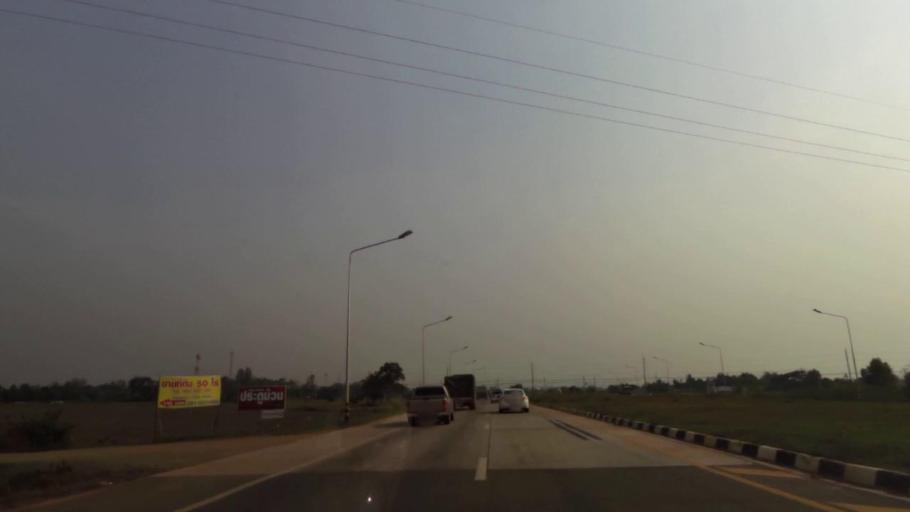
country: TH
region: Rayong
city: Klaeng
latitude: 12.7882
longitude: 101.6765
